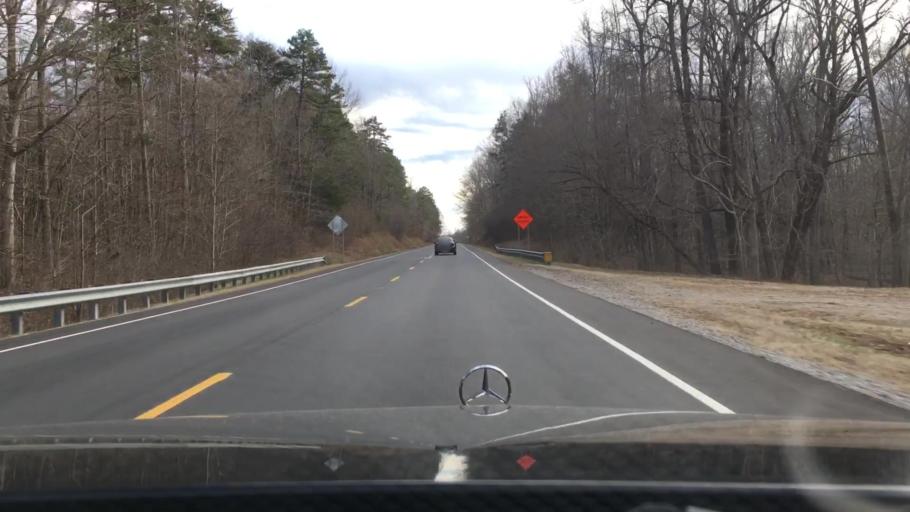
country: US
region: North Carolina
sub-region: Caswell County
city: Yanceyville
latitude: 36.4763
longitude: -79.3785
